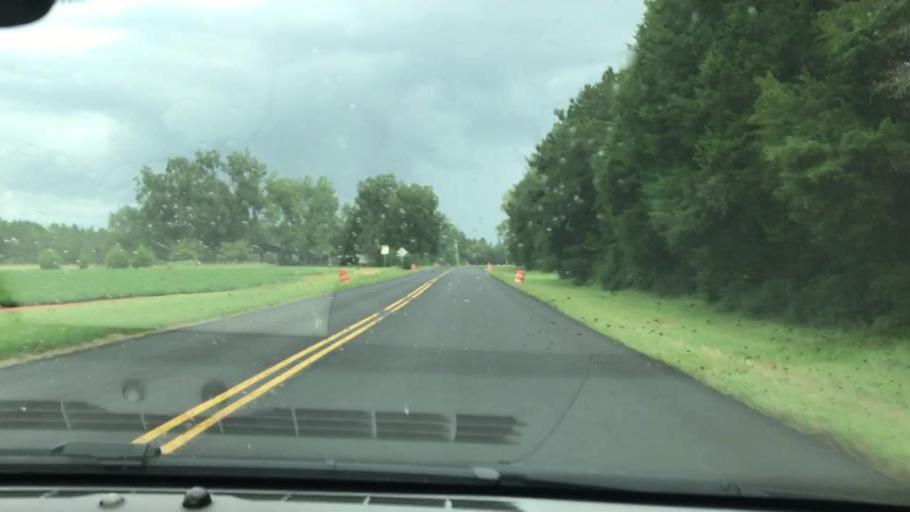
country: US
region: Georgia
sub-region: Clay County
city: Fort Gaines
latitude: 31.4814
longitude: -85.0174
